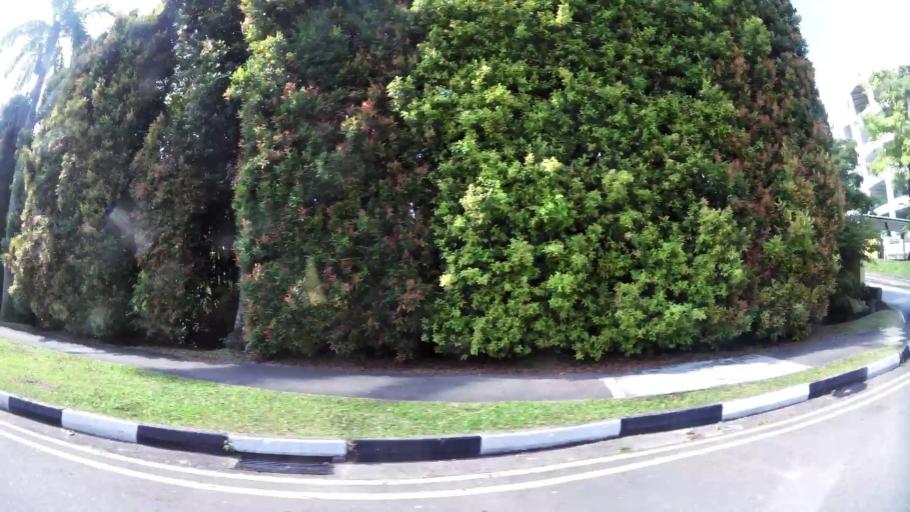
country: SG
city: Singapore
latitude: 1.3612
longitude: 103.8408
